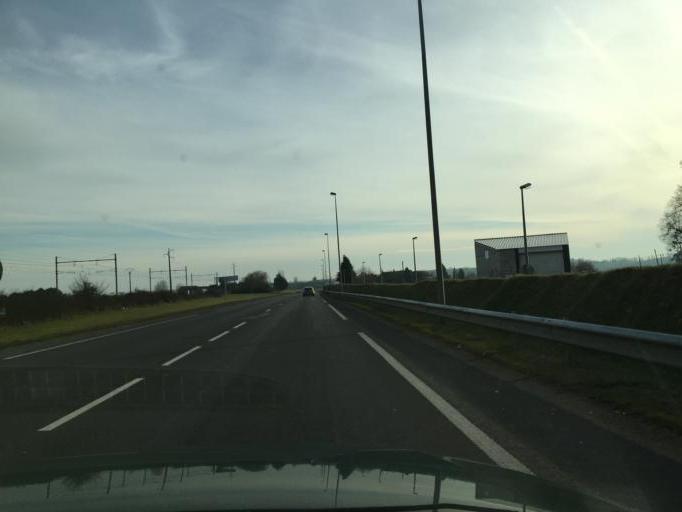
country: FR
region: Centre
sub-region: Departement du Loiret
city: Saint-Denis-en-Val
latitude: 47.8656
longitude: 1.9351
